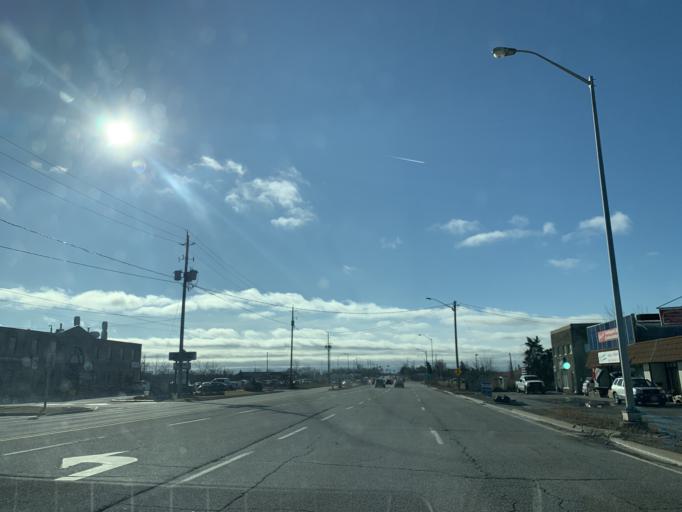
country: CA
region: Ontario
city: Hamilton
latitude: 43.3142
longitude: -79.9157
